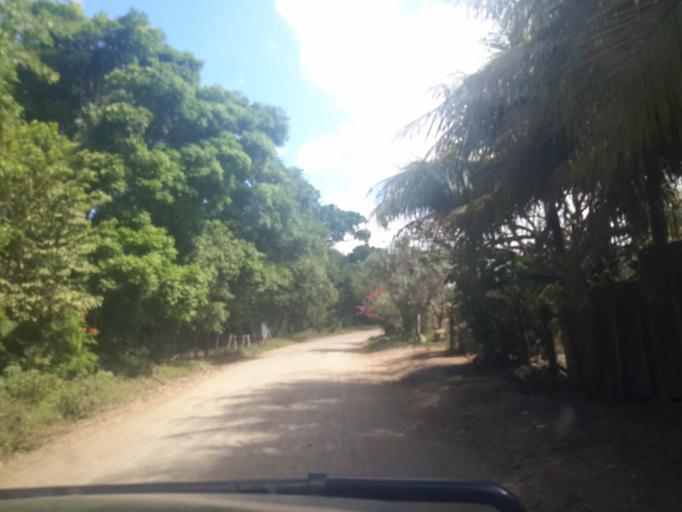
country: NI
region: Granada
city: Nandaime
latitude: 11.6658
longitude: -85.9489
